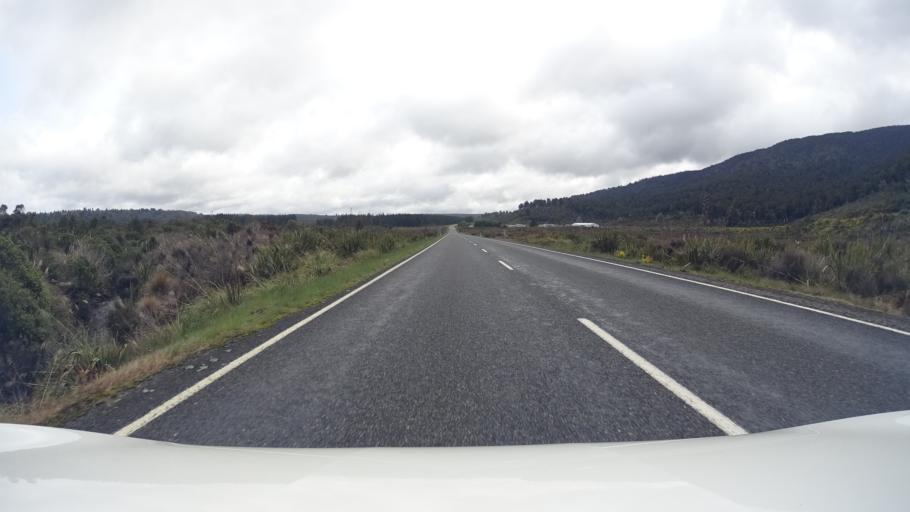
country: NZ
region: Manawatu-Wanganui
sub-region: Ruapehu District
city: Waiouru
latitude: -39.2328
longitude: 175.3934
